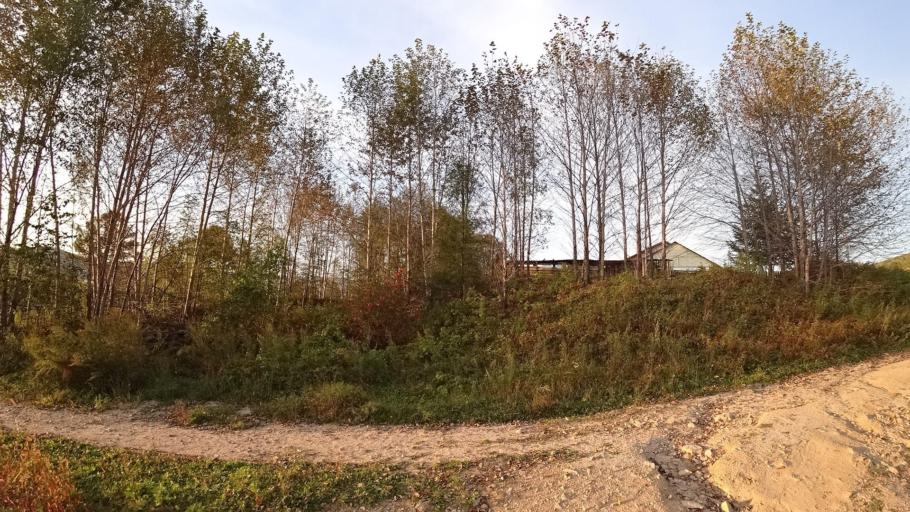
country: RU
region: Jewish Autonomous Oblast
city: Kul'dur
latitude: 49.1966
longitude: 131.6350
